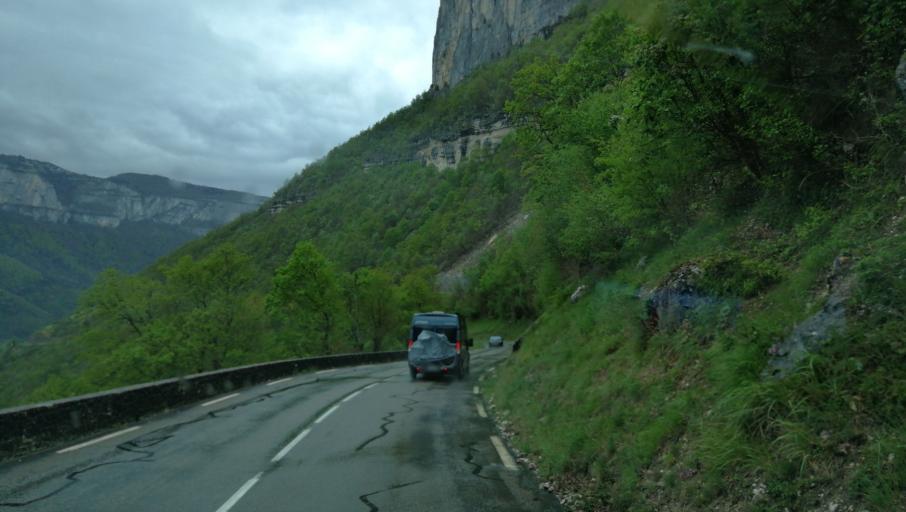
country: FR
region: Rhone-Alpes
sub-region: Departement de l'Isere
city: Pont-en-Royans
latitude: 45.0682
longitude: 5.4352
